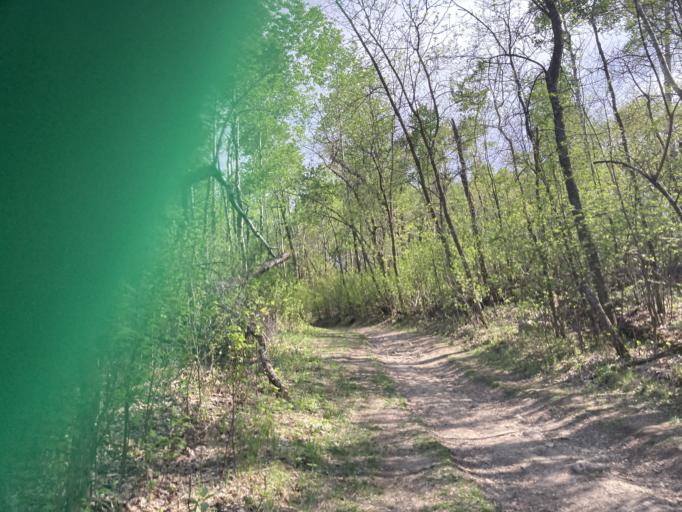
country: CA
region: Manitoba
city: Brandon
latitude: 49.7196
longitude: -99.9060
